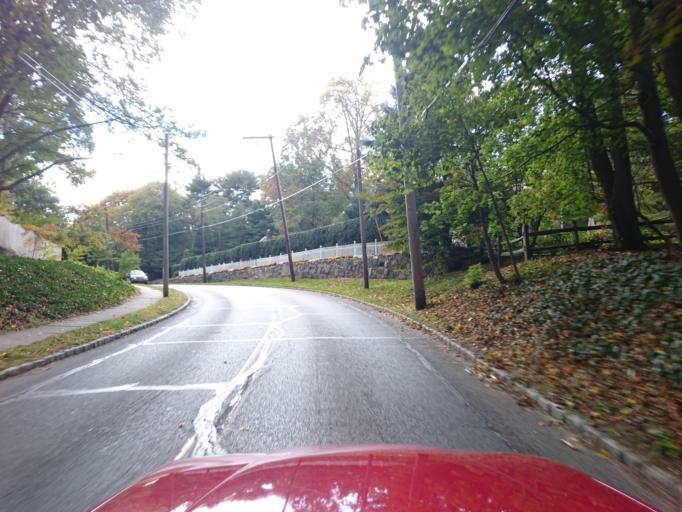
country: US
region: New York
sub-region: Nassau County
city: Locust Valley
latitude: 40.8824
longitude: -73.5956
